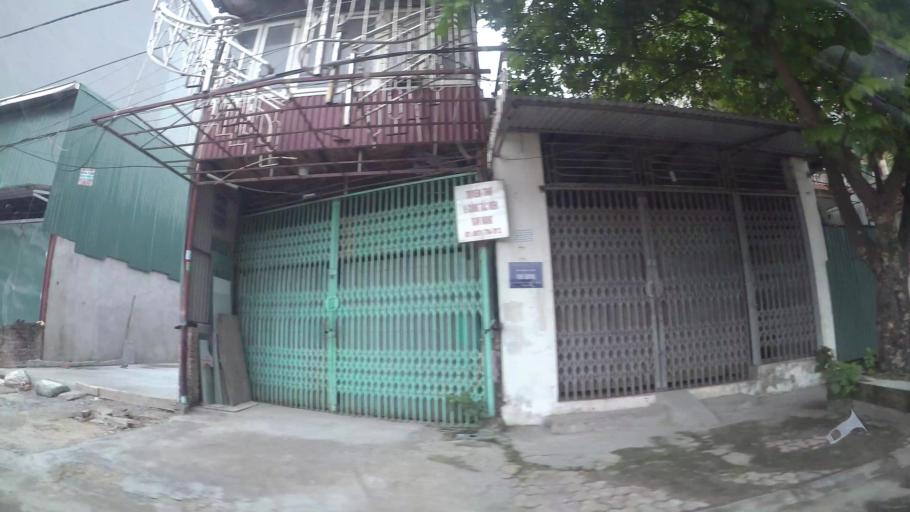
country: VN
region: Ha Noi
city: Van Dien
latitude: 20.9747
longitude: 105.8828
